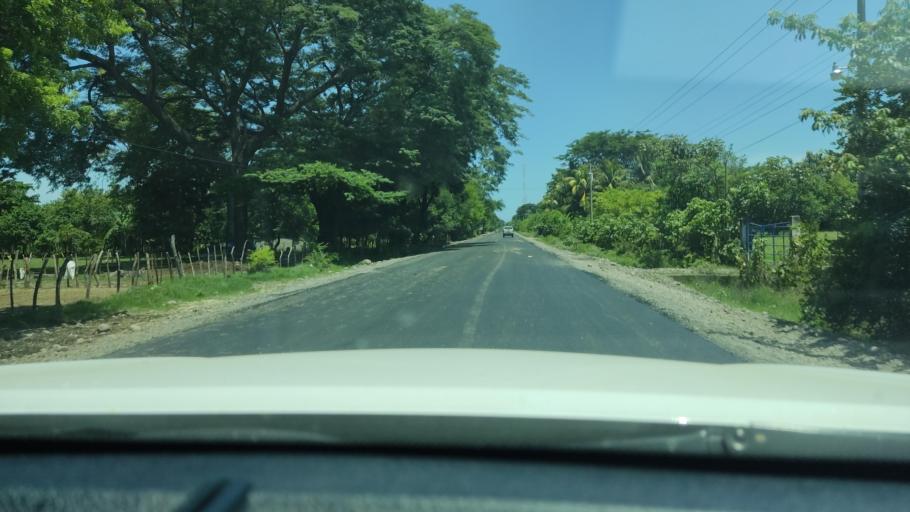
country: SV
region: Ahuachapan
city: San Francisco Menendez
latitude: 13.8333
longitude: -90.1194
